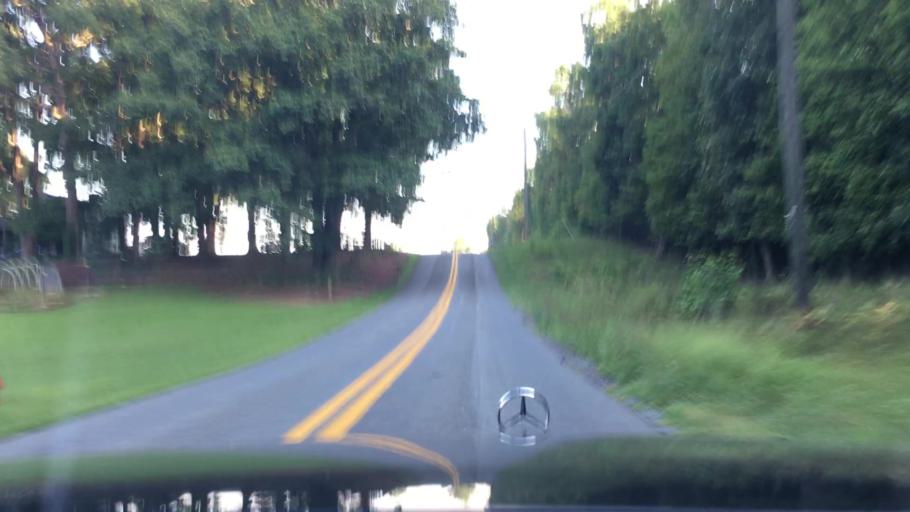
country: US
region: Virginia
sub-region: Campbell County
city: Timberlake
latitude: 37.2698
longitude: -79.2645
